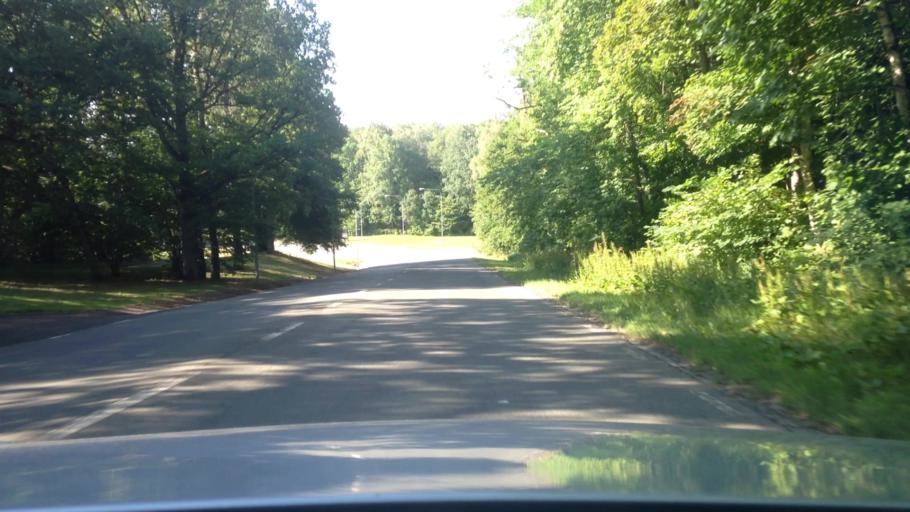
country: SE
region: Vaestra Goetaland
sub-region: Skovde Kommun
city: Skoevde
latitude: 58.3985
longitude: 13.8186
